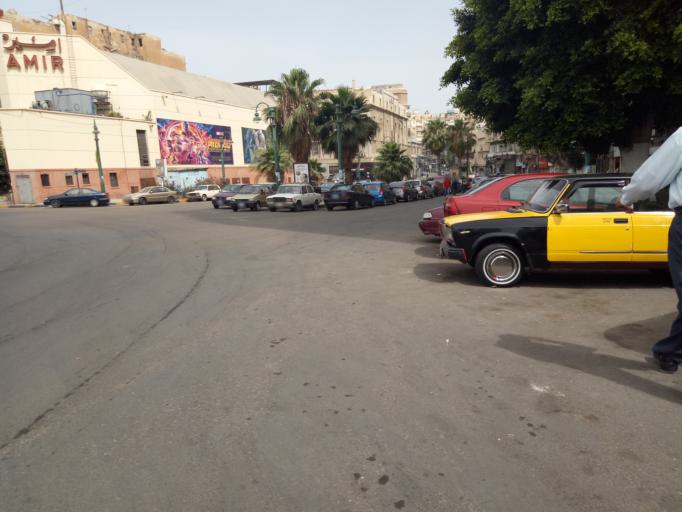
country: EG
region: Alexandria
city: Alexandria
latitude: 31.1965
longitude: 29.9048
